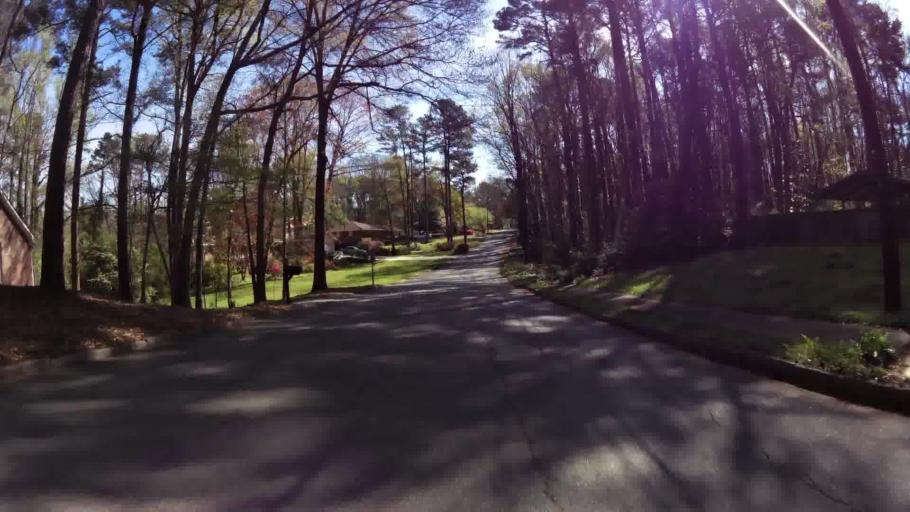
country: US
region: Georgia
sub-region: DeKalb County
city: Clarkston
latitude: 33.8261
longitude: -84.2620
